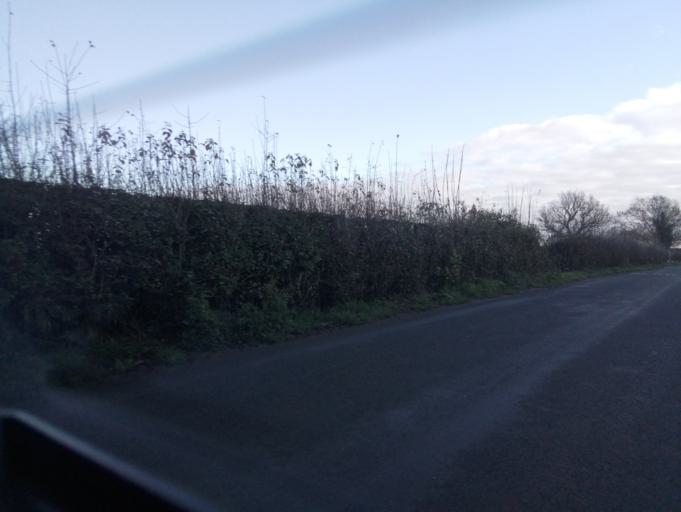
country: GB
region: England
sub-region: Staffordshire
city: Barton under Needwood
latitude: 52.8021
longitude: -1.7208
